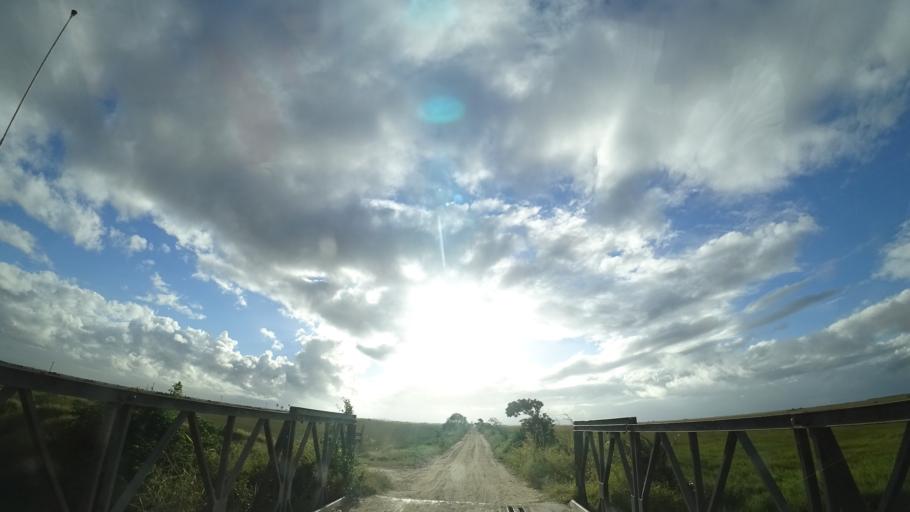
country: MZ
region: Sofala
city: Beira
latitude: -19.7565
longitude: 34.9227
